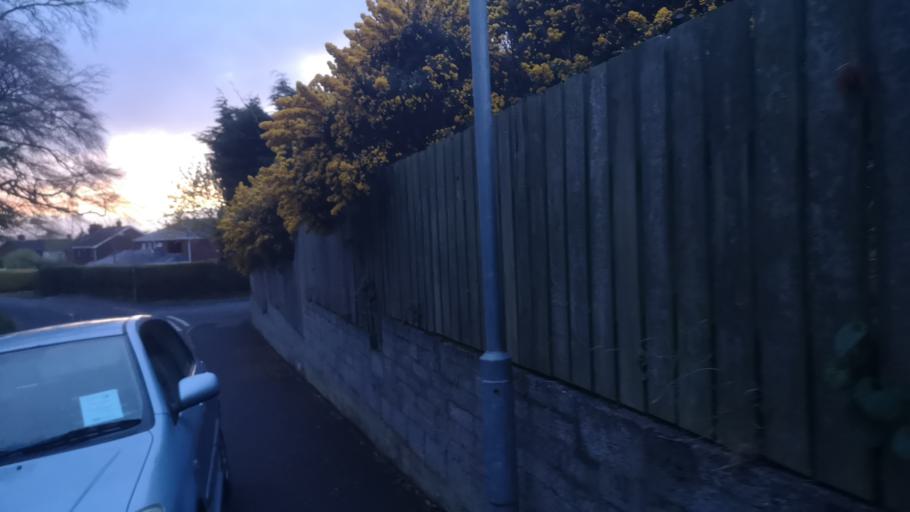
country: GB
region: Northern Ireland
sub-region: Newry and Mourne District
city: Newry
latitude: 54.1832
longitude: -6.3135
